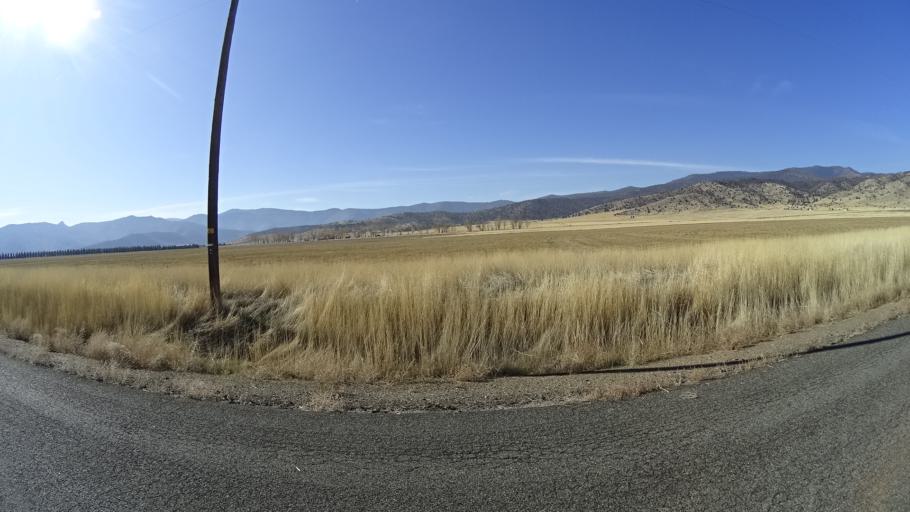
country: US
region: California
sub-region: Siskiyou County
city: Montague
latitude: 41.5610
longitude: -122.5473
